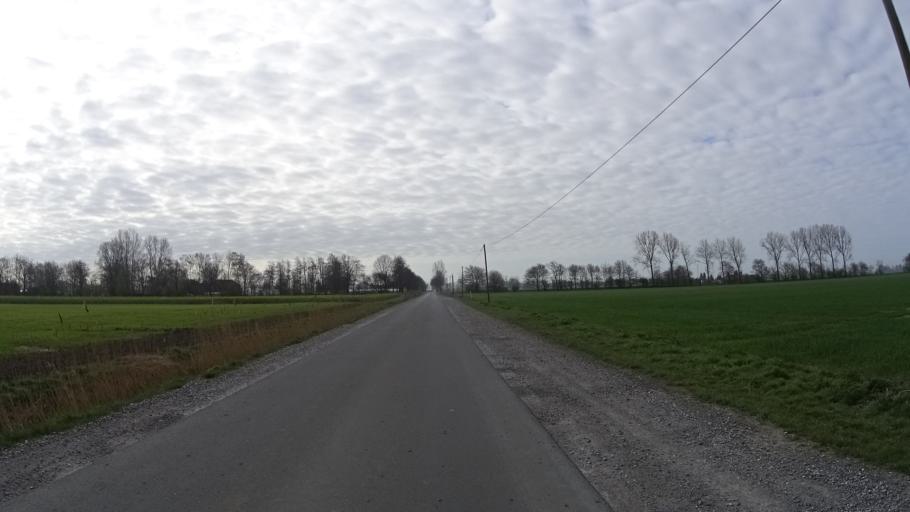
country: DE
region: Lower Saxony
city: Emden
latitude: 53.3982
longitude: 7.3265
